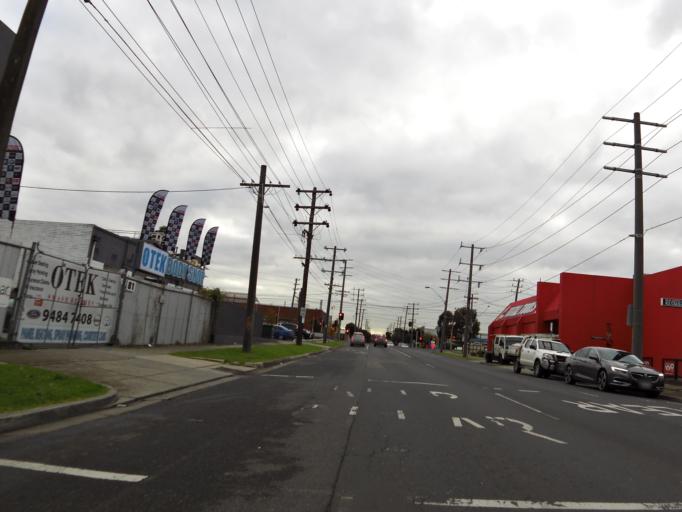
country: AU
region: Victoria
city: Heidelberg West
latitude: -37.7491
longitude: 145.0296
